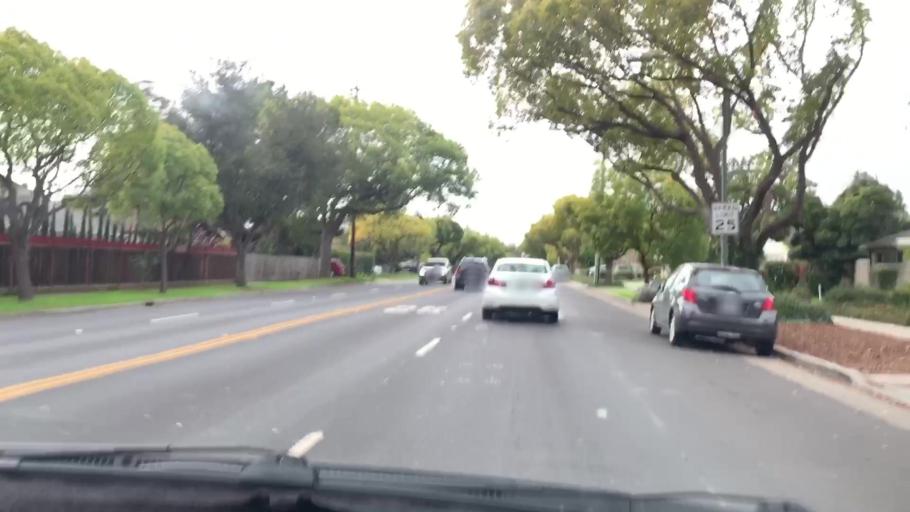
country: US
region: California
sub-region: Santa Clara County
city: Palo Alto
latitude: 37.4445
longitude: -122.1351
